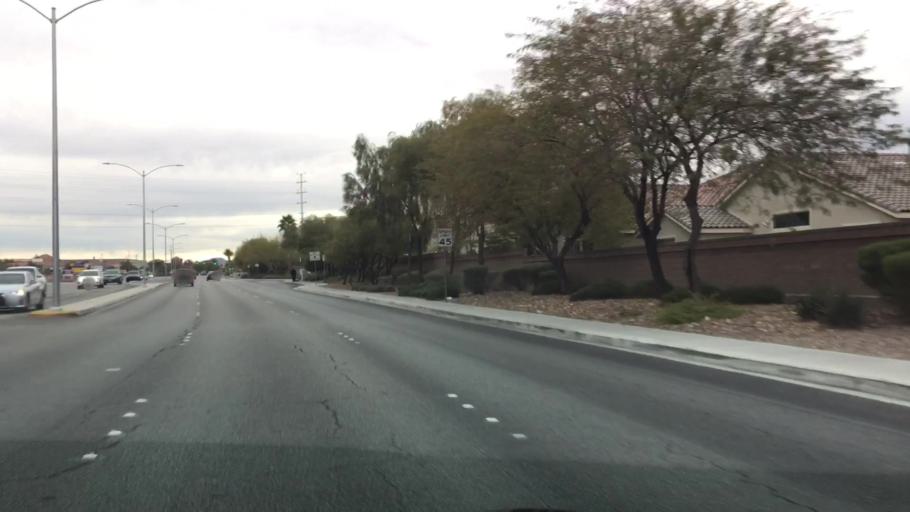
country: US
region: Nevada
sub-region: Clark County
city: Whitney
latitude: 36.0050
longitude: -115.0993
